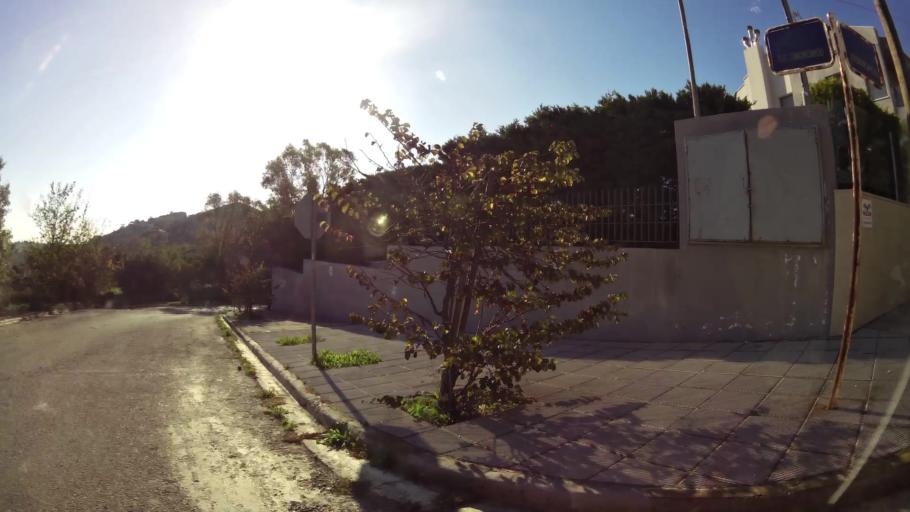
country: GR
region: Attica
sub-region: Nomarchia Anatolikis Attikis
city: Dhrafi
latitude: 38.0229
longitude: 23.9104
